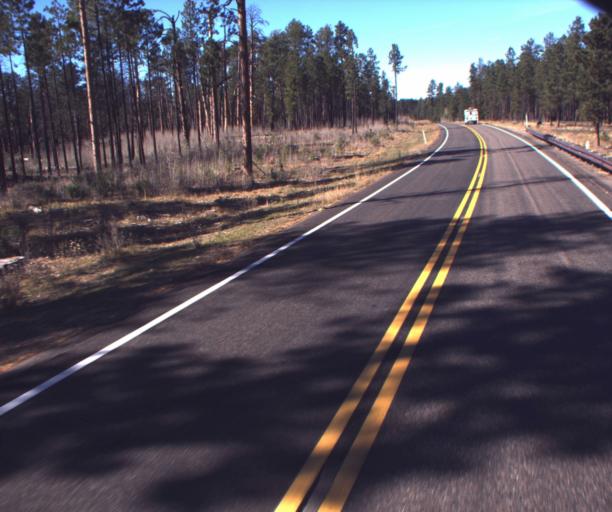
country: US
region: Arizona
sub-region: Coconino County
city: Fredonia
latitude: 36.6783
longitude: -112.2106
